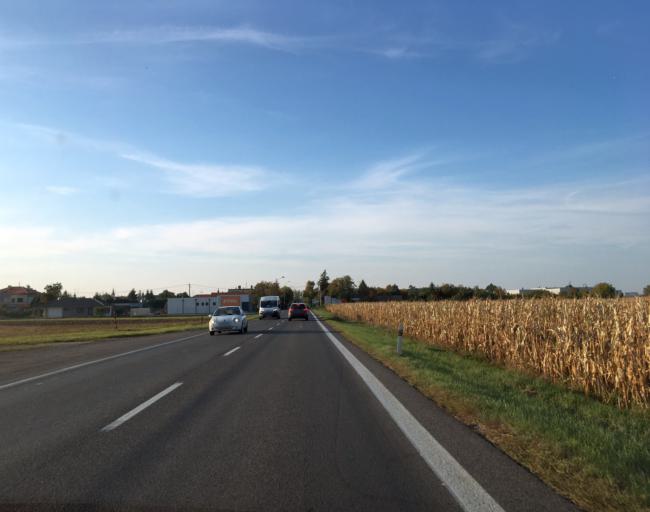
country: SK
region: Nitriansky
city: Sellye
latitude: 48.1648
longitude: 17.9013
